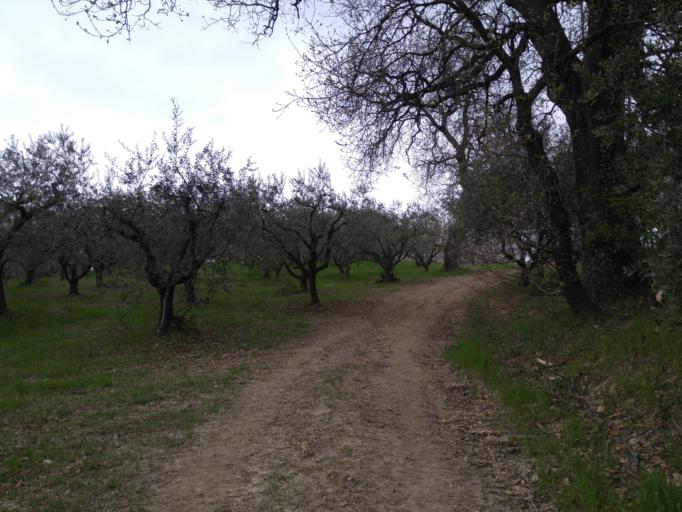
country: IT
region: The Marches
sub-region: Provincia di Pesaro e Urbino
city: Calcinelli
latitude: 43.7655
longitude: 12.9088
